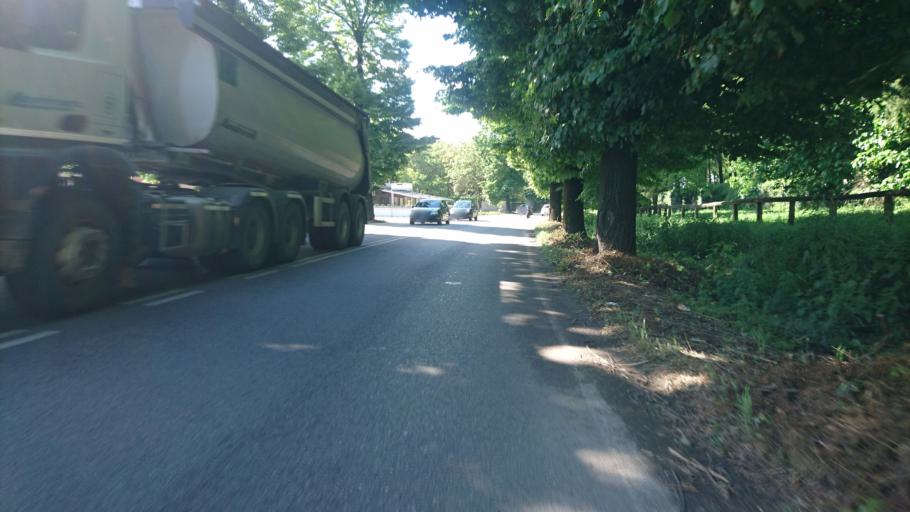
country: IT
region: Veneto
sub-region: Provincia di Padova
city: Monselice
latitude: 45.2419
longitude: 11.7599
